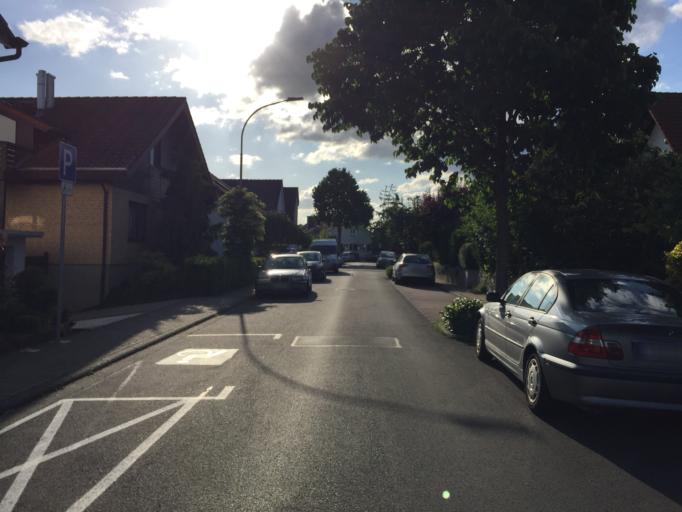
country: DE
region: Hesse
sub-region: Regierungsbezirk Darmstadt
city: Karben
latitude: 50.2270
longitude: 8.7711
